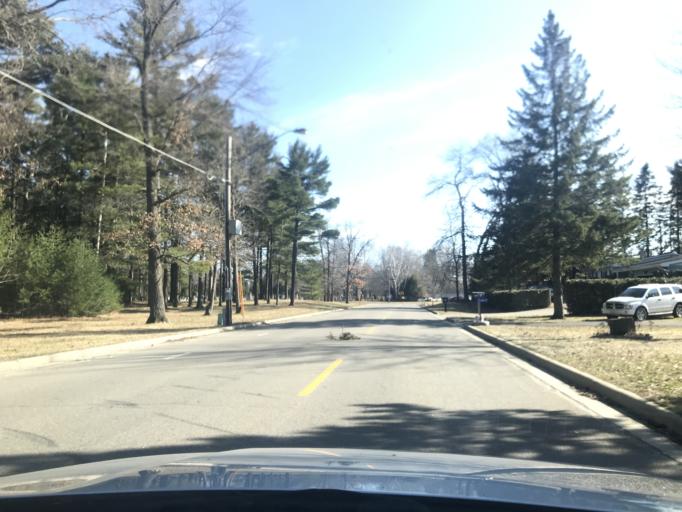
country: US
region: Wisconsin
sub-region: Marinette County
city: Marinette
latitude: 45.0899
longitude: -87.6398
